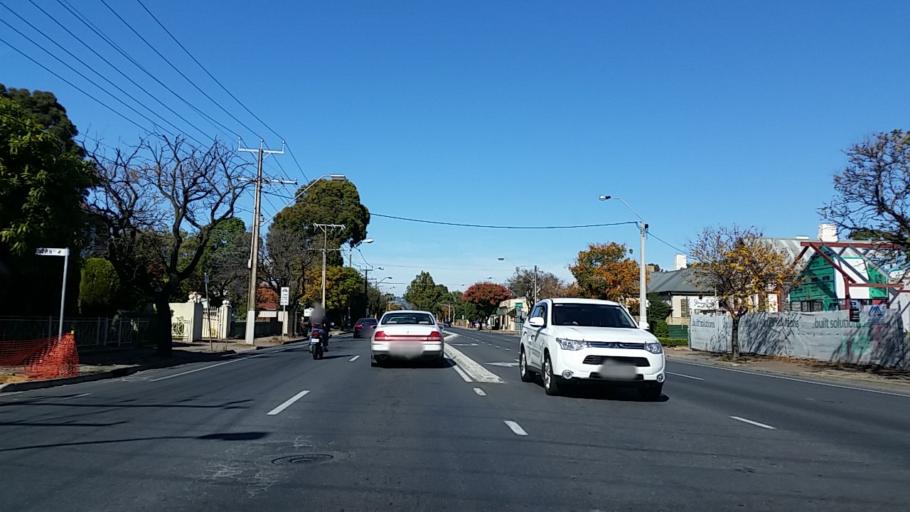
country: AU
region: South Australia
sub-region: Norwood Payneham St Peters
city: Payneham
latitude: -34.9002
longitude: 138.6395
